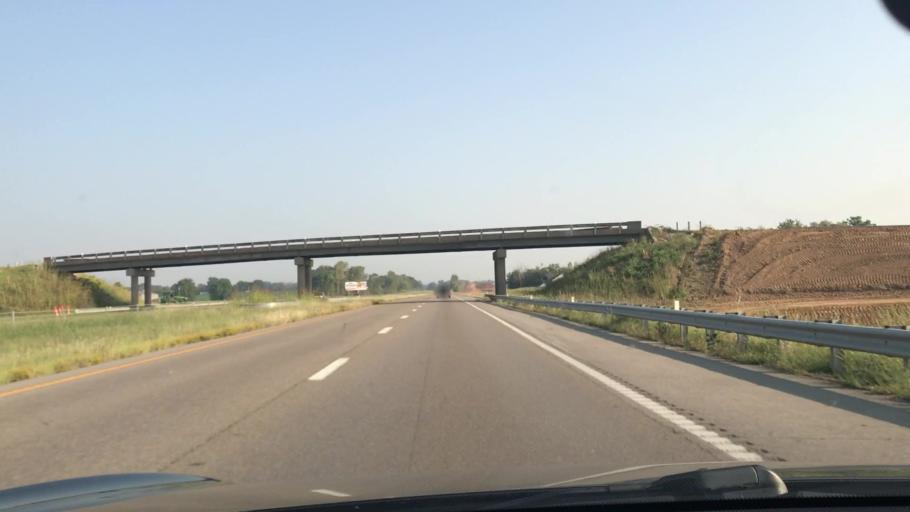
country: US
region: Missouri
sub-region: Scott County
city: Scott City
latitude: 37.1819
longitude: -89.5374
